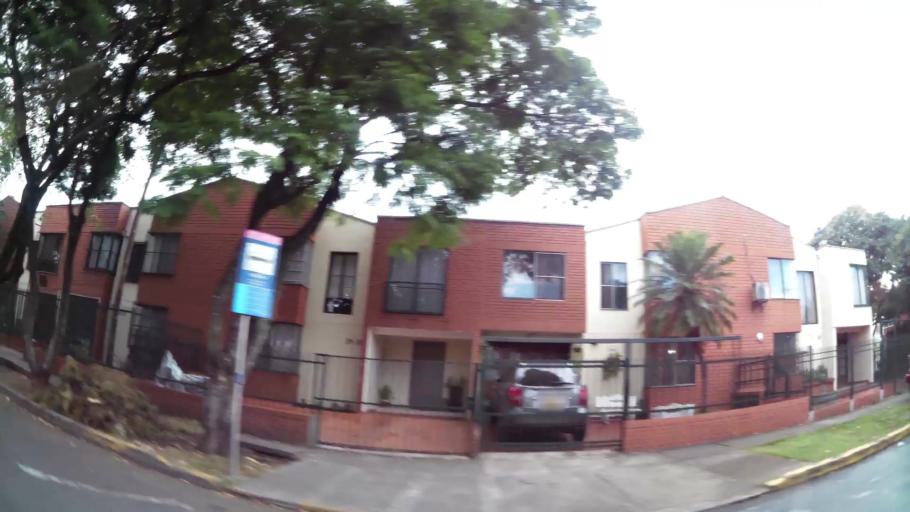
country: CO
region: Valle del Cauca
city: Cali
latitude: 3.4886
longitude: -76.5157
